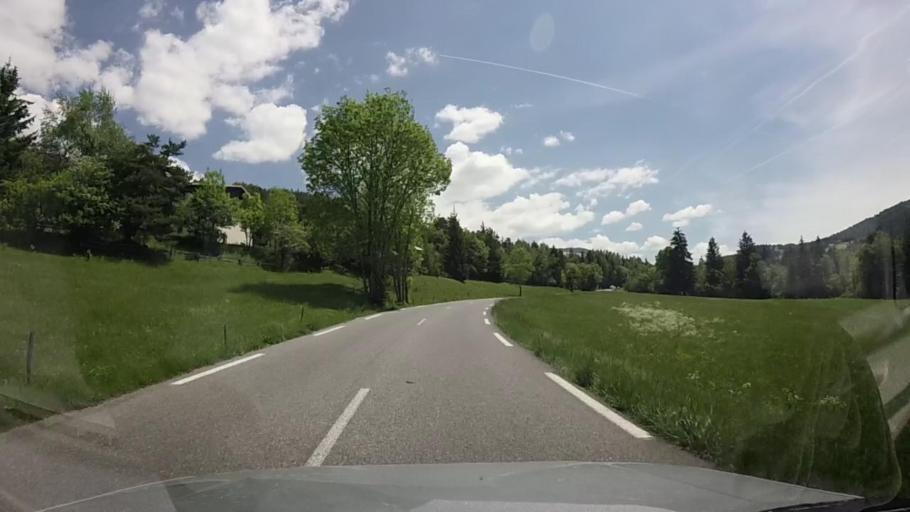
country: FR
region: Provence-Alpes-Cote d'Azur
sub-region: Departement des Alpes-de-Haute-Provence
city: Seyne-les-Alpes
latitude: 44.3336
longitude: 6.3893
